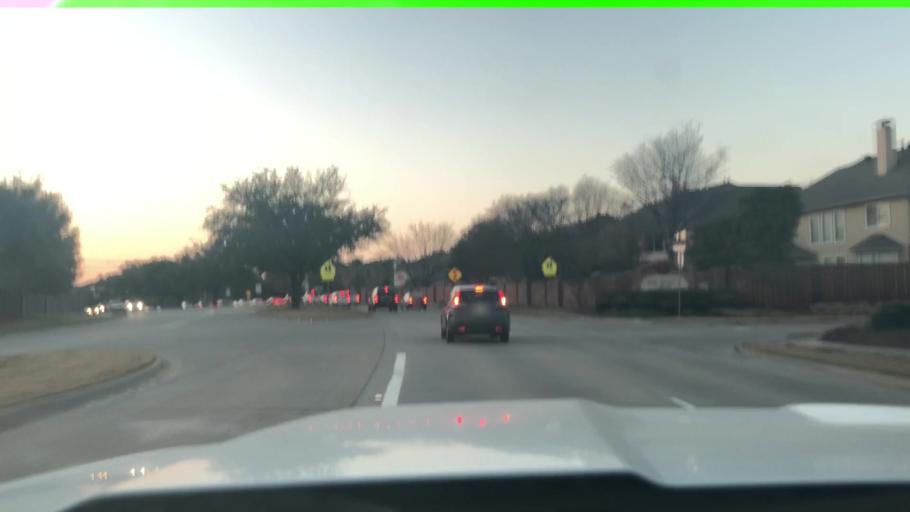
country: US
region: Texas
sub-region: Denton County
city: Flower Mound
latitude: 33.0210
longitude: -97.0774
